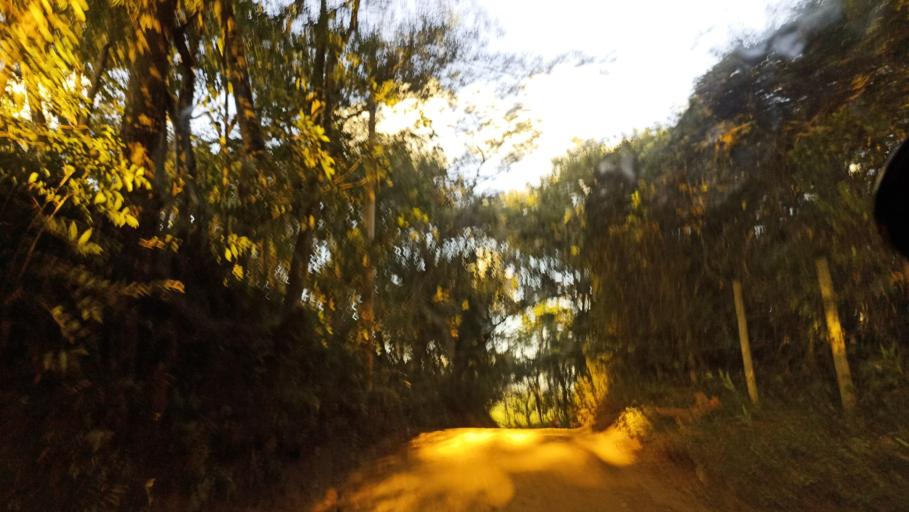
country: BR
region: Minas Gerais
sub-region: Sao Joao Del Rei
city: Sao Joao del Rei
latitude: -21.1836
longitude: -44.3473
